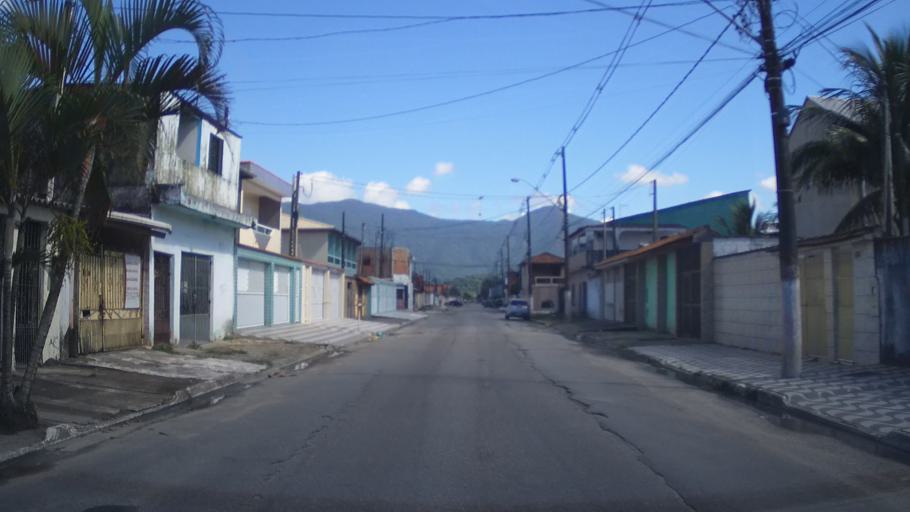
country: BR
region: Sao Paulo
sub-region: Mongagua
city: Mongagua
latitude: -24.0367
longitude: -46.5199
